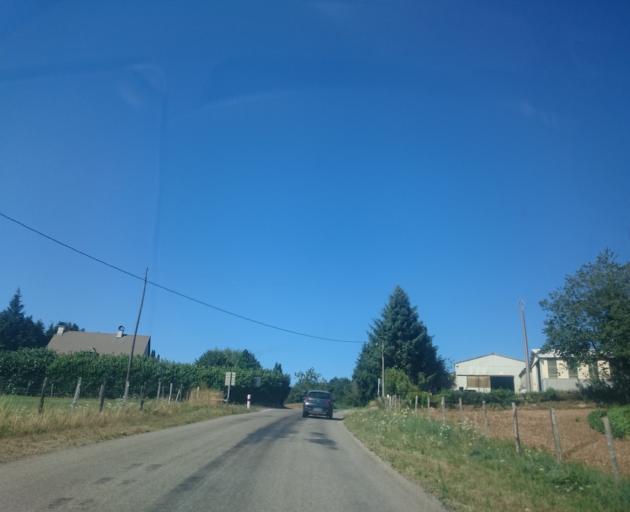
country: FR
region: Auvergne
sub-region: Departement du Cantal
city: Saint-Mamet-la-Salvetat
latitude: 44.8079
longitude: 2.3667
